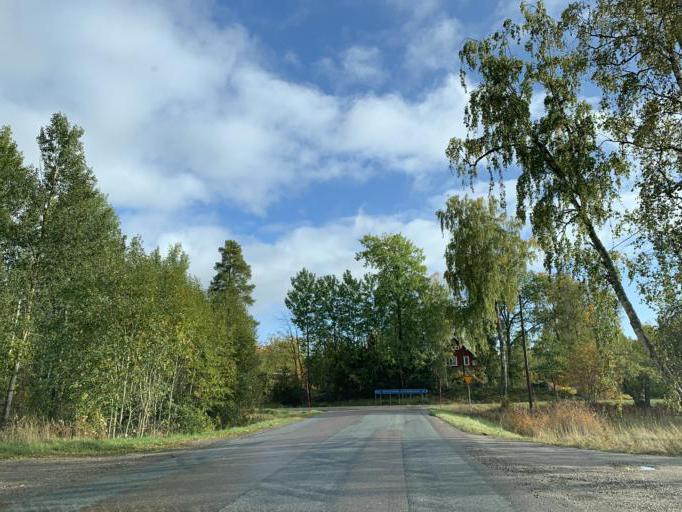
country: SE
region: Soedermanland
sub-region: Eskilstuna Kommun
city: Kvicksund
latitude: 59.3151
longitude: 16.2727
